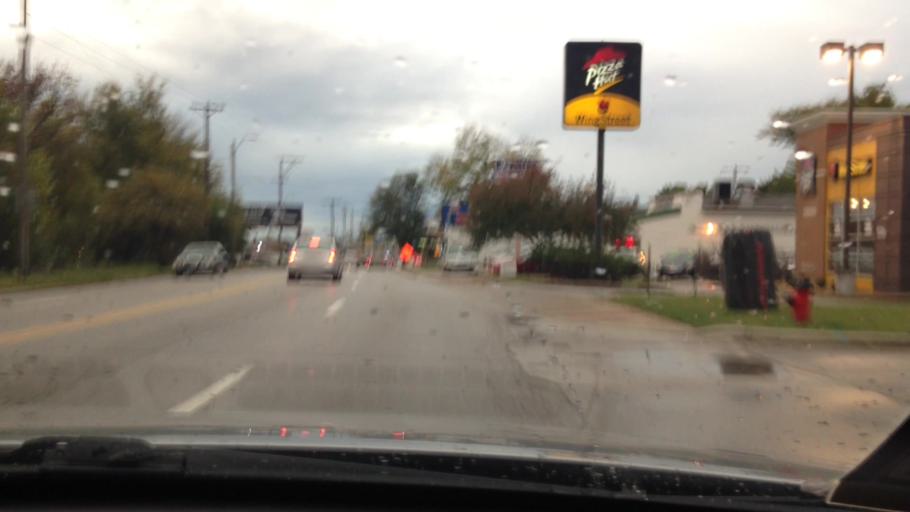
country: US
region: Kansas
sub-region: Johnson County
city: Leawood
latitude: 38.9898
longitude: -94.5945
